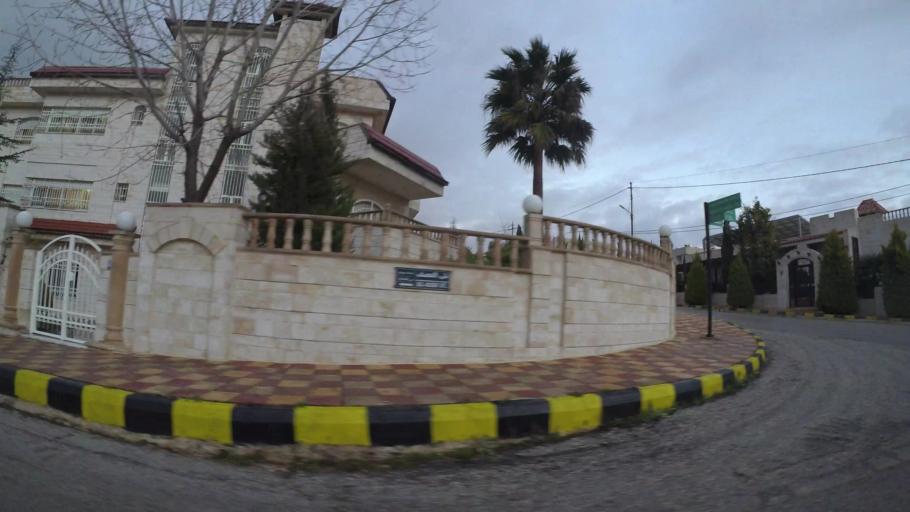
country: JO
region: Amman
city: Al Jubayhah
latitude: 32.0300
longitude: 35.8085
